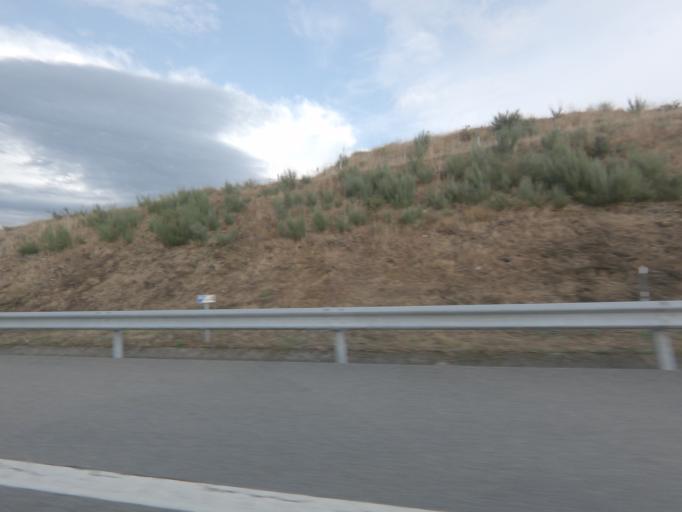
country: PT
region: Viseu
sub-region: Castro Daire
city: Castro Daire
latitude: 40.9806
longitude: -7.8828
